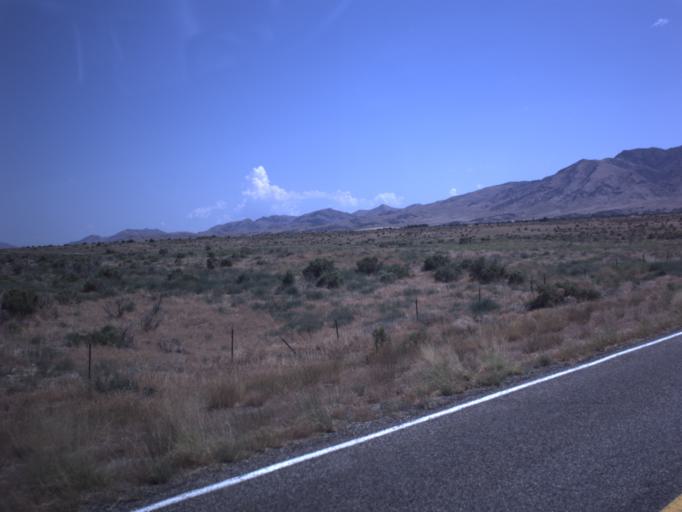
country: US
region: Utah
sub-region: Millard County
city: Delta
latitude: 39.3546
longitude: -112.3948
